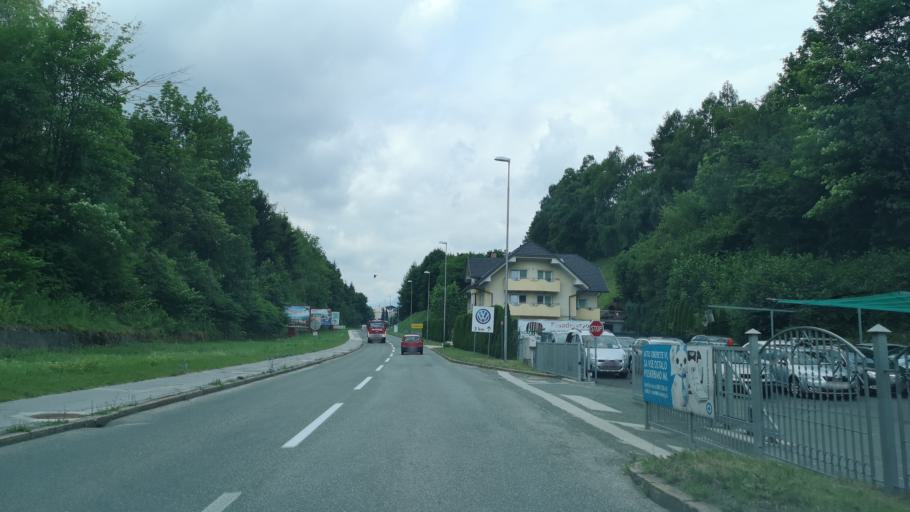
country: SI
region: Jesenice
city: Slovenski Javornik
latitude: 46.4289
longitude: 14.0780
